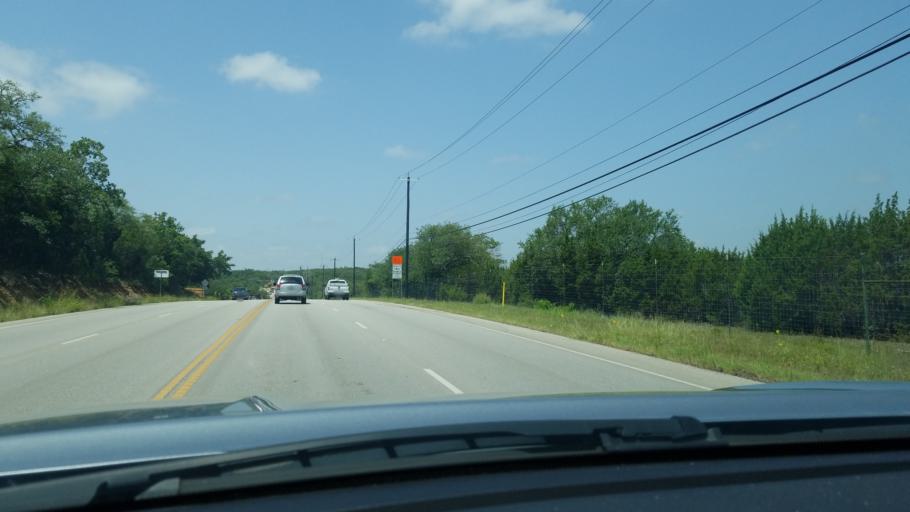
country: US
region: Texas
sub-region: Bexar County
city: Timberwood Park
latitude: 29.7115
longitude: -98.4807
